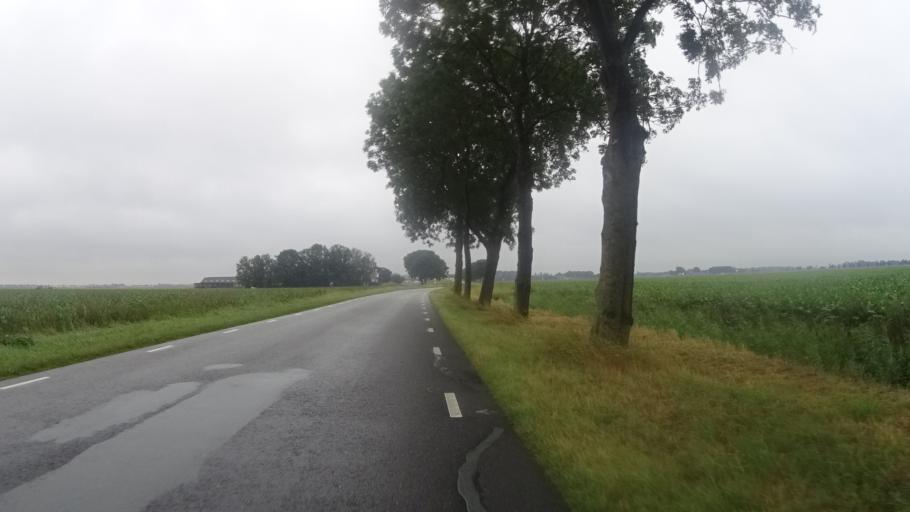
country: NL
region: Groningen
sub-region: Gemeente Veendam
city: Veendam
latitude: 53.1882
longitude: 6.9365
